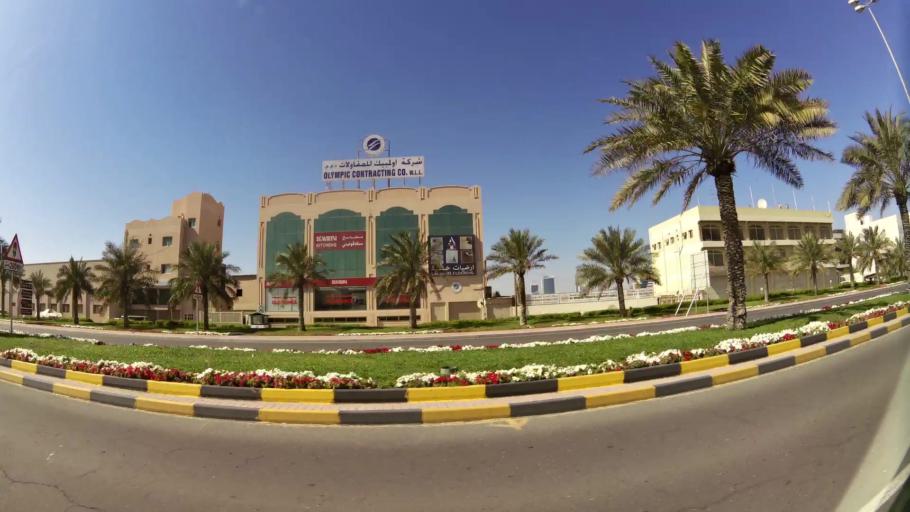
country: BH
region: Muharraq
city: Al Muharraq
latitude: 26.2466
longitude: 50.6085
